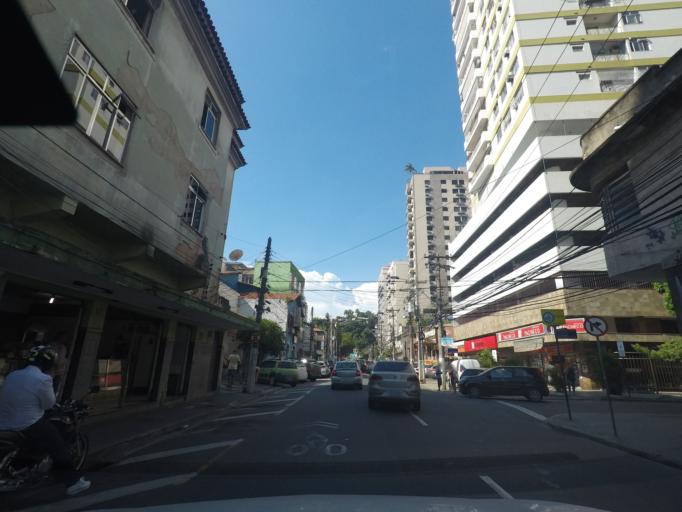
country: BR
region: Rio de Janeiro
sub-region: Niteroi
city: Niteroi
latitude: -22.9037
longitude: -43.1222
